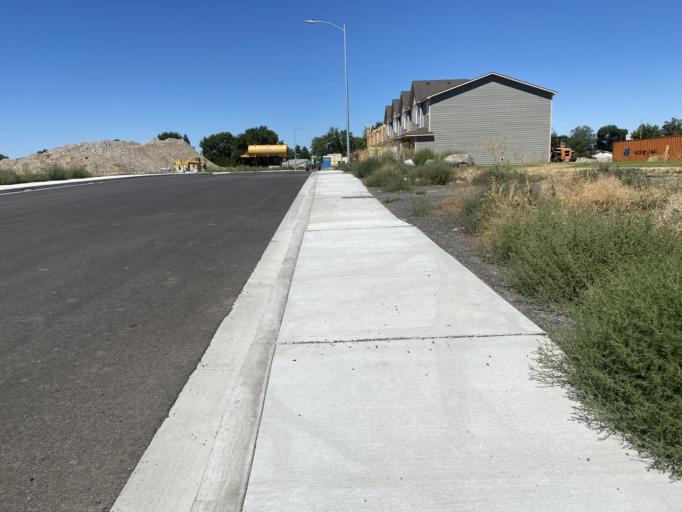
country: US
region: Washington
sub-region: Benton County
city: Kennewick
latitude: 46.2031
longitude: -119.1745
